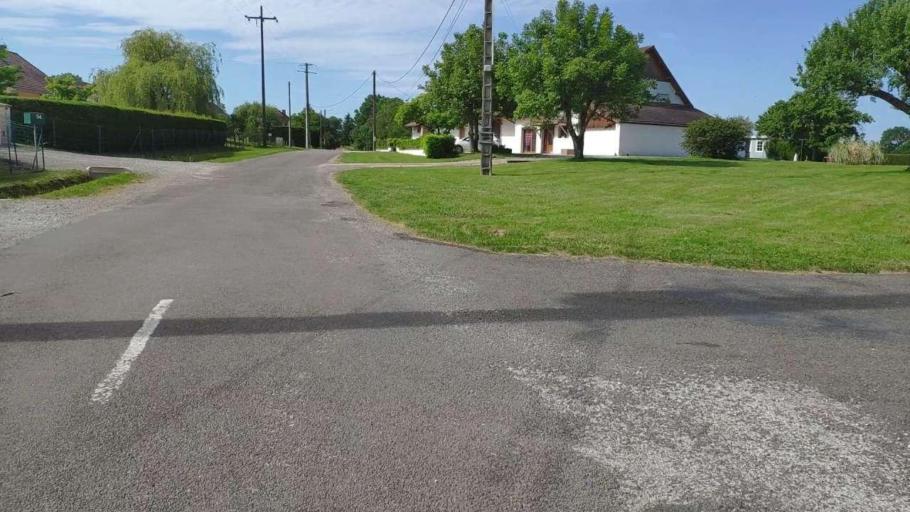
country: FR
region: Franche-Comte
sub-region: Departement du Jura
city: Bletterans
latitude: 46.7133
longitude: 5.4584
